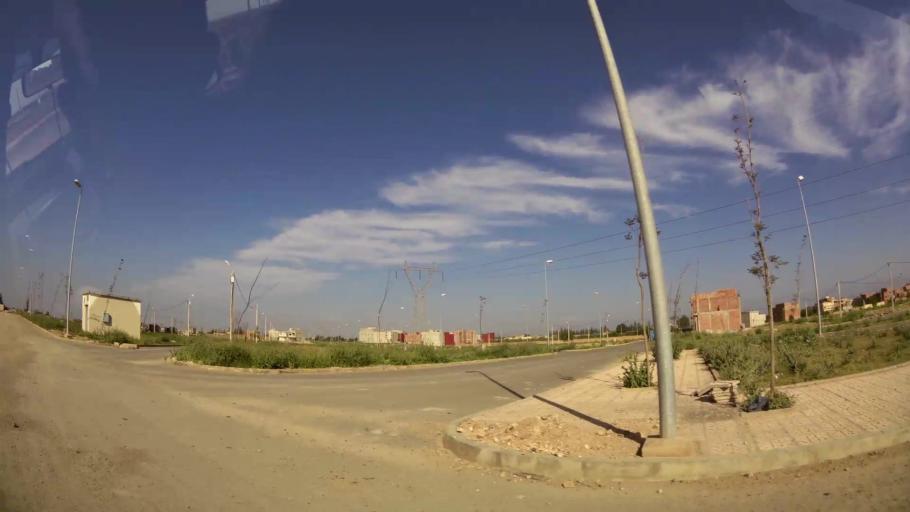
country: MA
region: Oriental
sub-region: Oujda-Angad
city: Oujda
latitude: 34.7243
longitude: -1.8850
